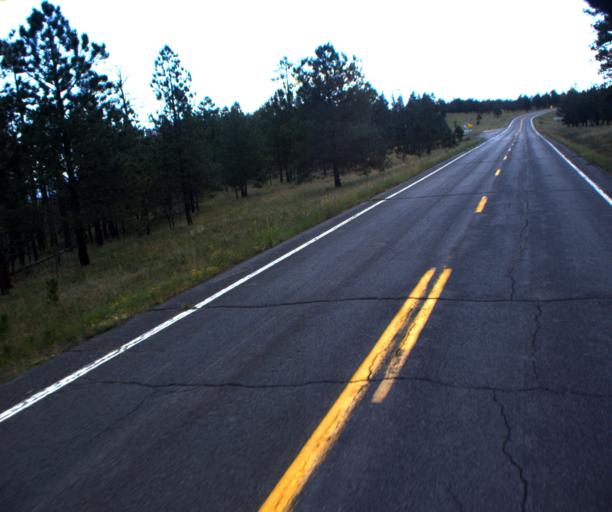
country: US
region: Arizona
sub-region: Apache County
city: Eagar
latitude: 34.0435
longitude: -109.3522
